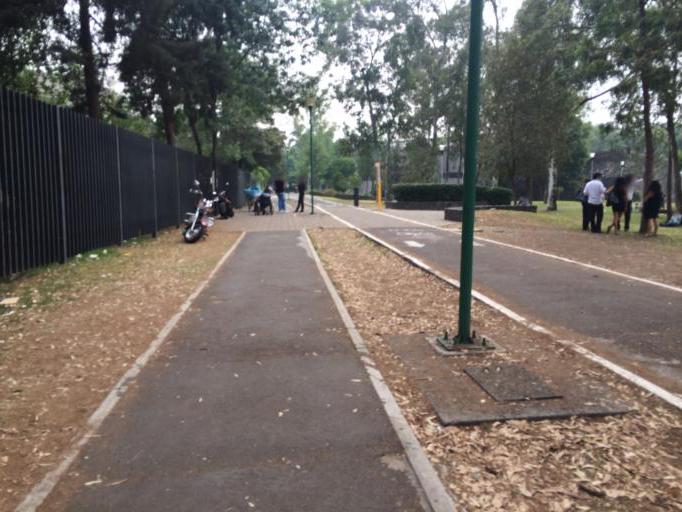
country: MX
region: Mexico City
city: Magdalena Contreras
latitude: 19.3257
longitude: -99.1845
